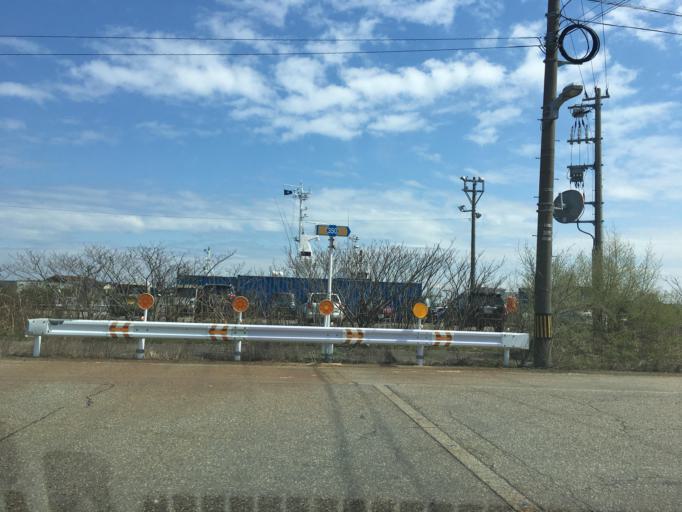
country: JP
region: Toyama
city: Nishishinminato
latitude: 36.7913
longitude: 137.0650
